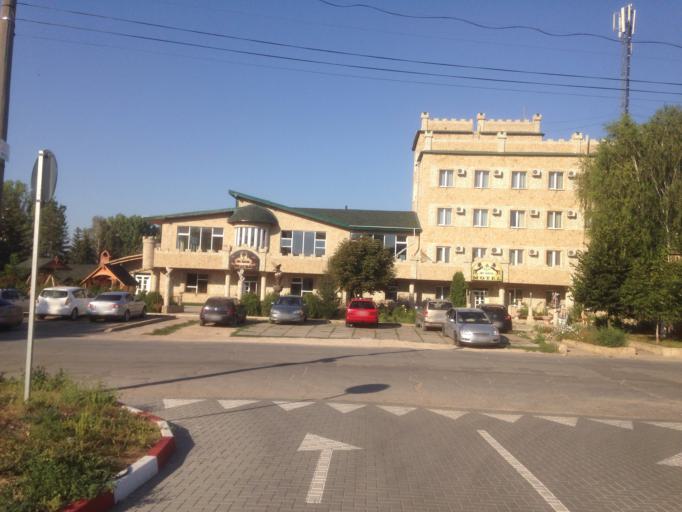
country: MD
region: Ungheni
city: Ungheni
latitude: 47.2258
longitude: 27.7936
